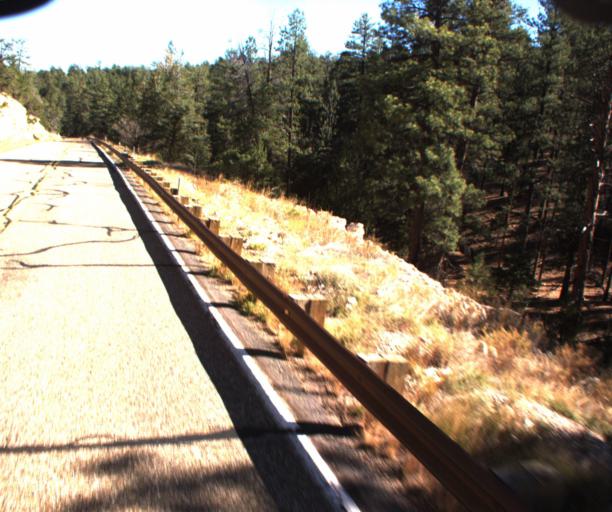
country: US
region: Arizona
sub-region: Coconino County
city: Fredonia
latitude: 36.7332
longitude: -112.1642
